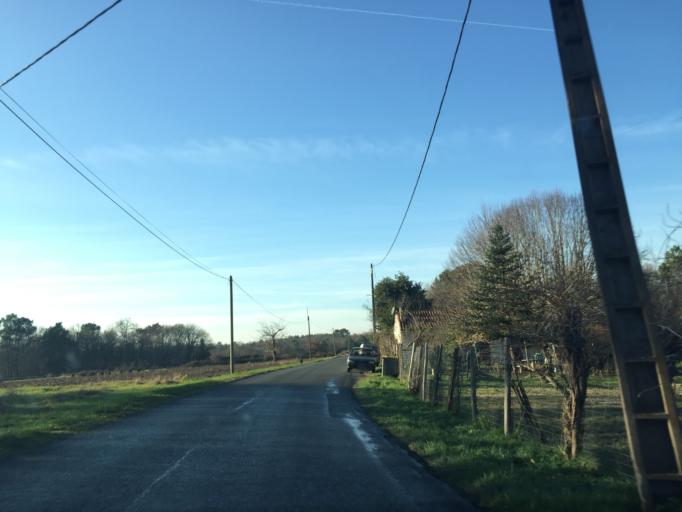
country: FR
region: Aquitaine
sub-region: Departement de la Dordogne
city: Riberac
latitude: 45.2025
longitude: 0.3200
